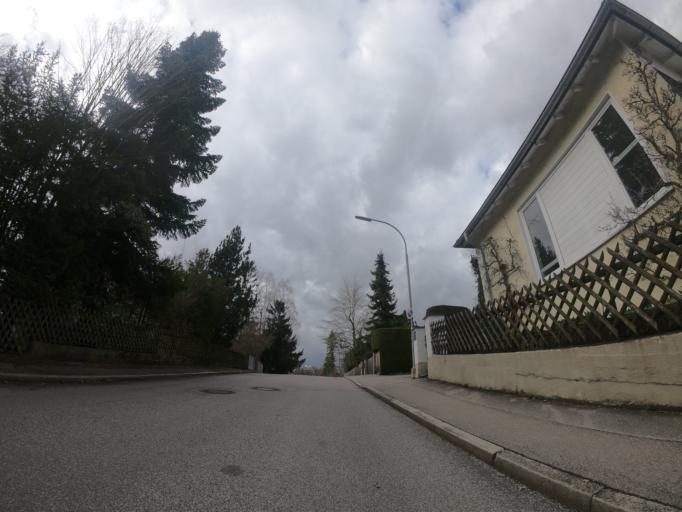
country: DE
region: Bavaria
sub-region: Upper Bavaria
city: Fuerstenfeldbruck
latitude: 48.1674
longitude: 11.2356
